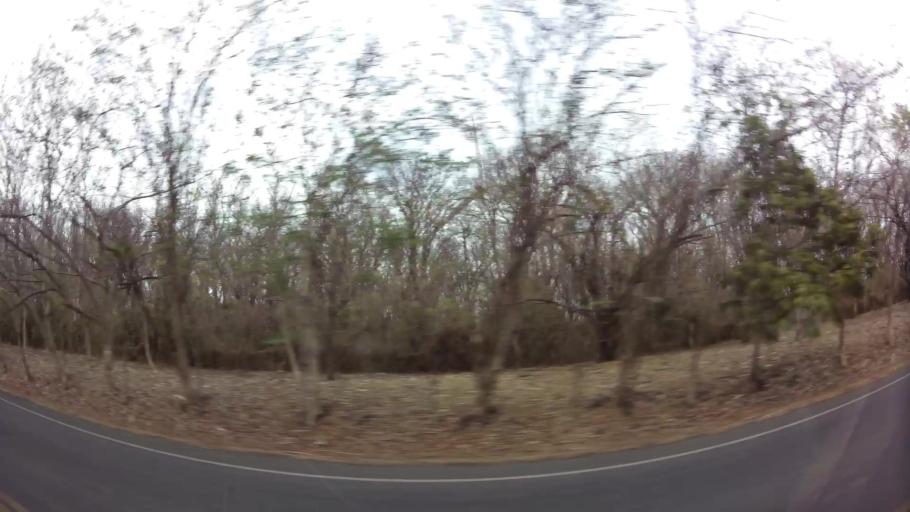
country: NI
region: Rivas
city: Rivas
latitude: 11.3390
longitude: -85.7304
